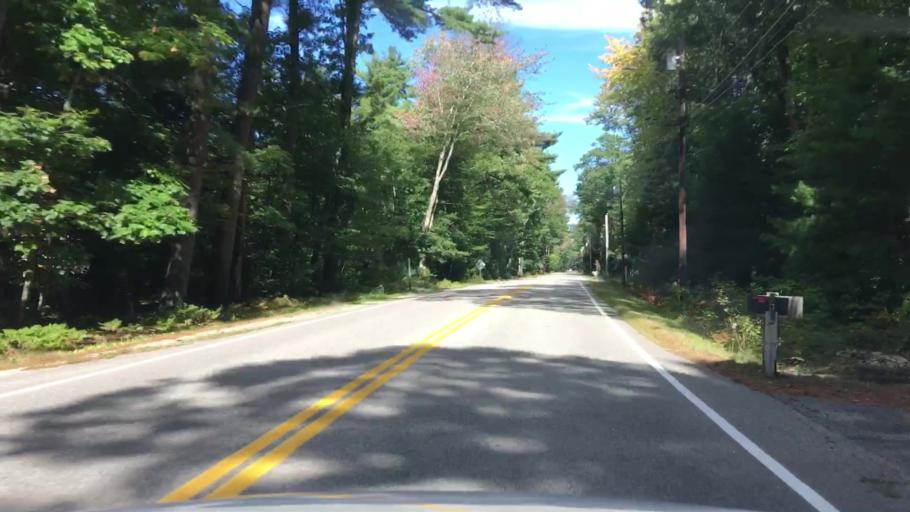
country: US
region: Maine
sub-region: Cumberland County
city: Westbrook
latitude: 43.6328
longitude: -70.4064
